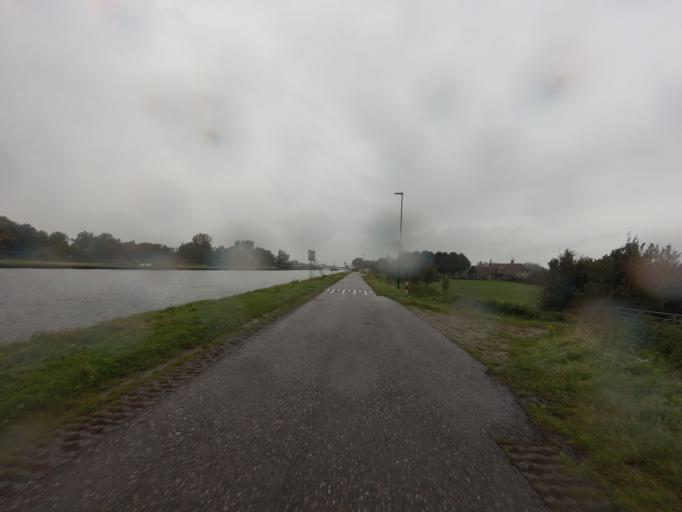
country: NL
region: South Holland
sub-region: Gemeente Gorinchem
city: Gorinchem
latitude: 51.8703
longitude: 4.9981
